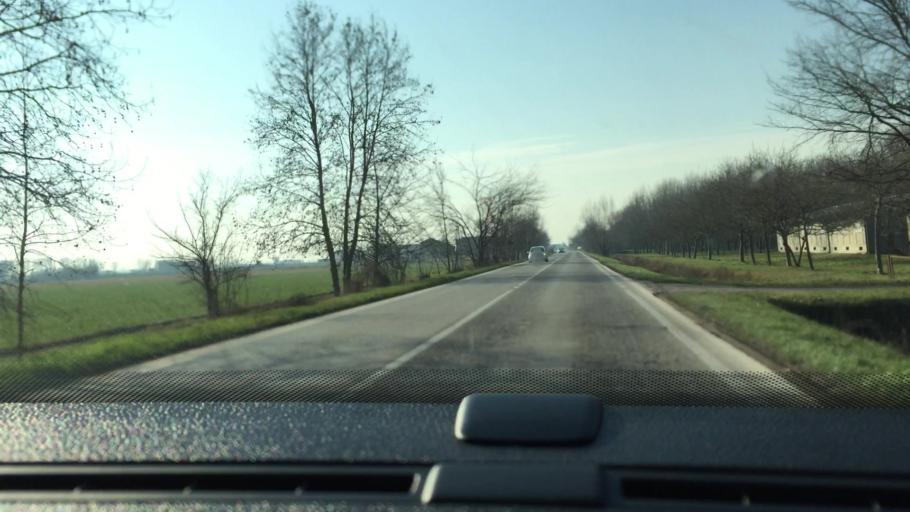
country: IT
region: Lombardy
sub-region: Provincia di Mantova
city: Goito
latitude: 45.2392
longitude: 10.6458
